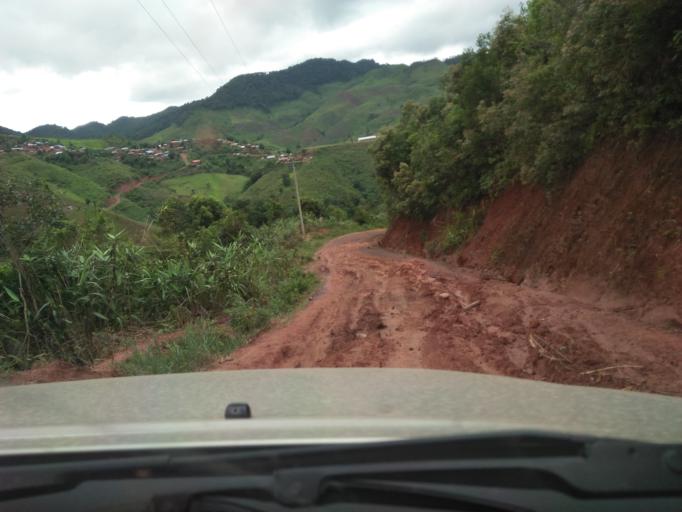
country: TH
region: Nan
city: Bo Kluea
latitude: 19.3773
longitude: 101.2137
